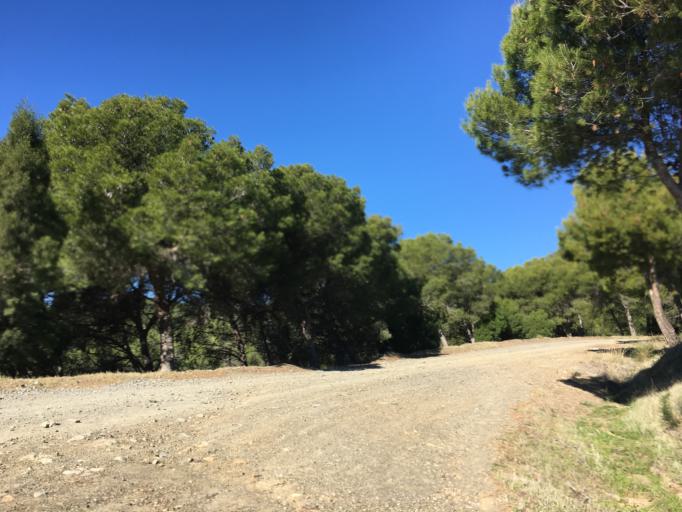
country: ES
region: Andalusia
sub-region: Provincia de Malaga
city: Malaga
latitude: 36.7805
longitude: -4.3893
